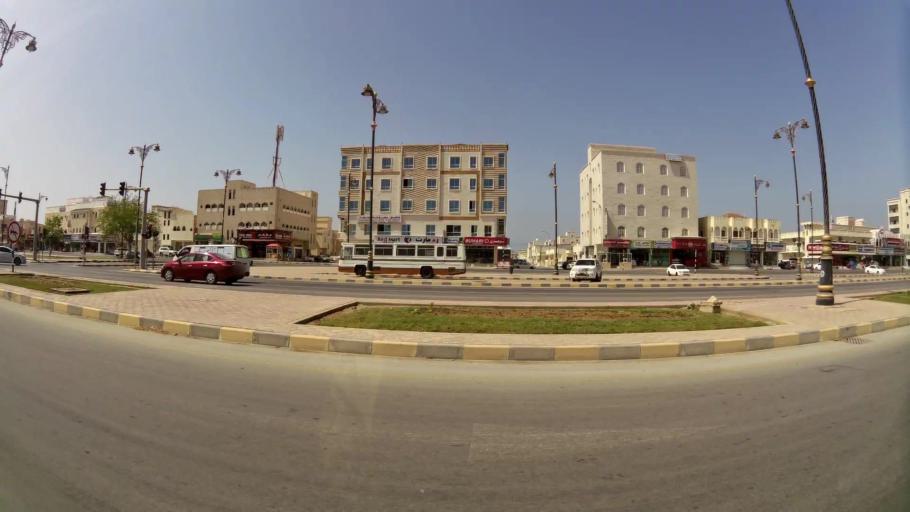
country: OM
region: Zufar
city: Salalah
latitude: 17.0263
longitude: 54.1575
